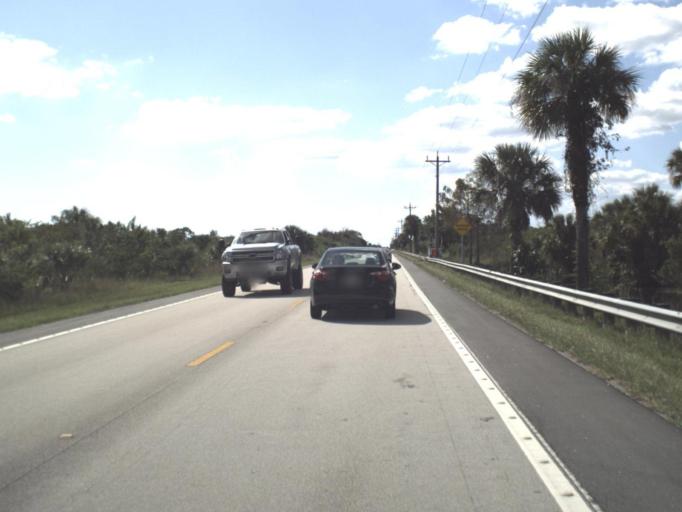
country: US
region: Florida
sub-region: Collier County
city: Marco
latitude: 25.9016
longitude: -81.3014
